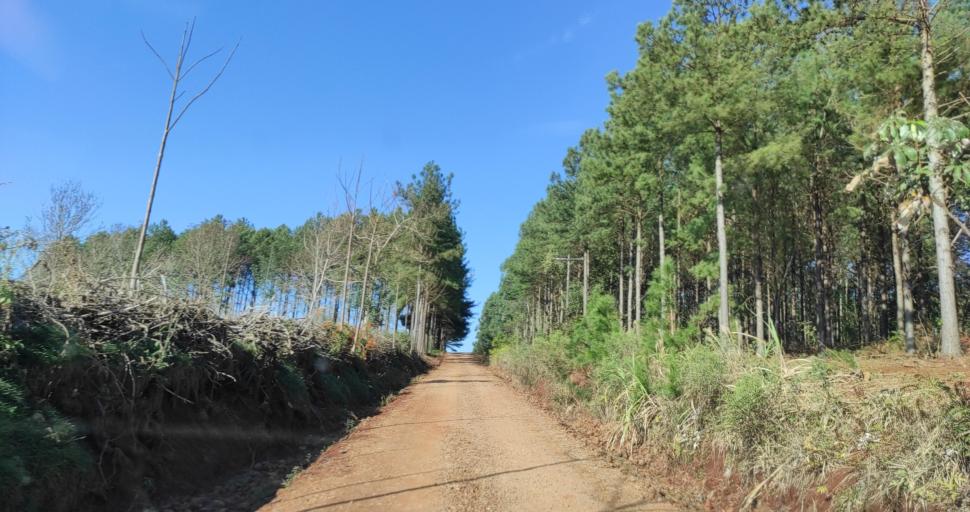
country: AR
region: Misiones
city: Capiovi
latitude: -26.8871
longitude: -55.0377
